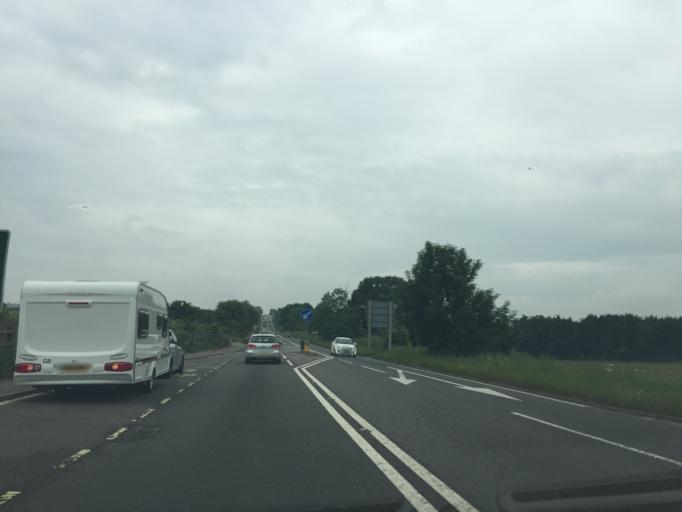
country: GB
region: England
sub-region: Dorset
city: Dorchester
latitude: 50.6920
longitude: -2.4532
